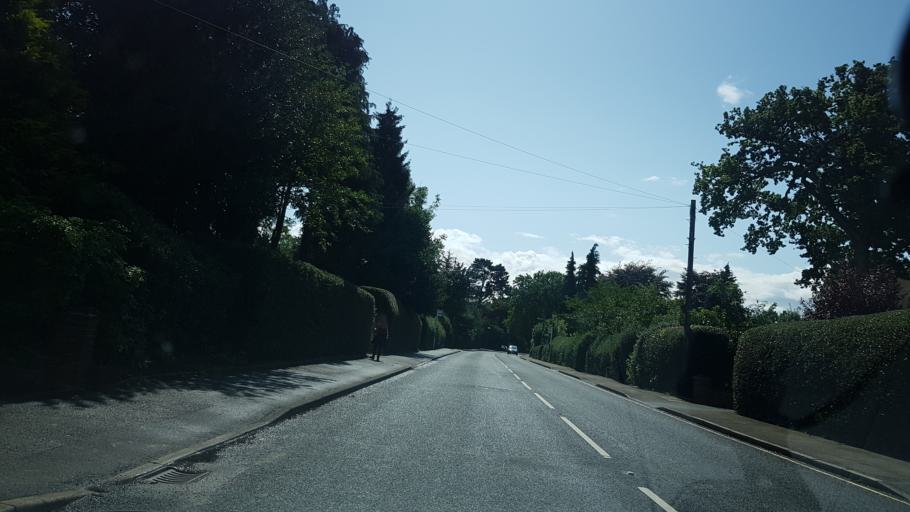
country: GB
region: England
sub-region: Surrey
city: West Byfleet
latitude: 51.3313
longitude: -0.5084
